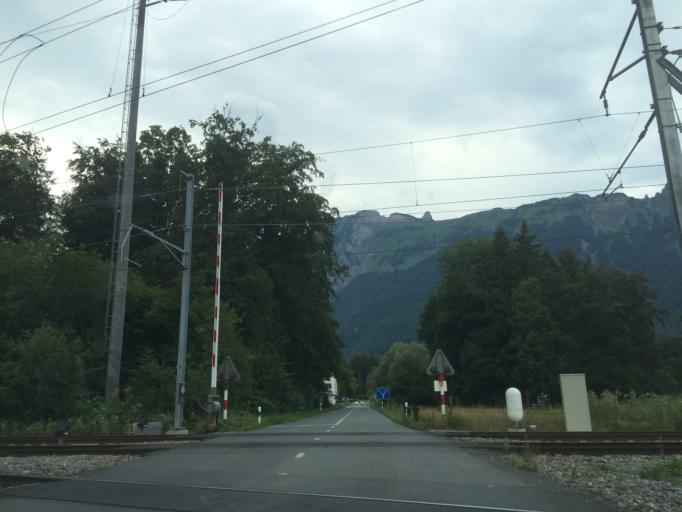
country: CH
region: Saint Gallen
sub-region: Wahlkreis Werdenberg
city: Sennwald
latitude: 47.2454
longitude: 9.5057
